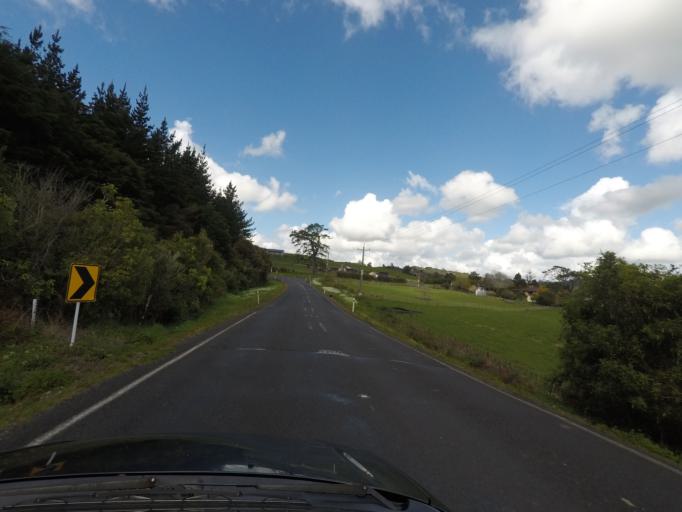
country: NZ
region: Auckland
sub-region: Auckland
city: Pukekohe East
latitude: -37.1446
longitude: 175.0166
